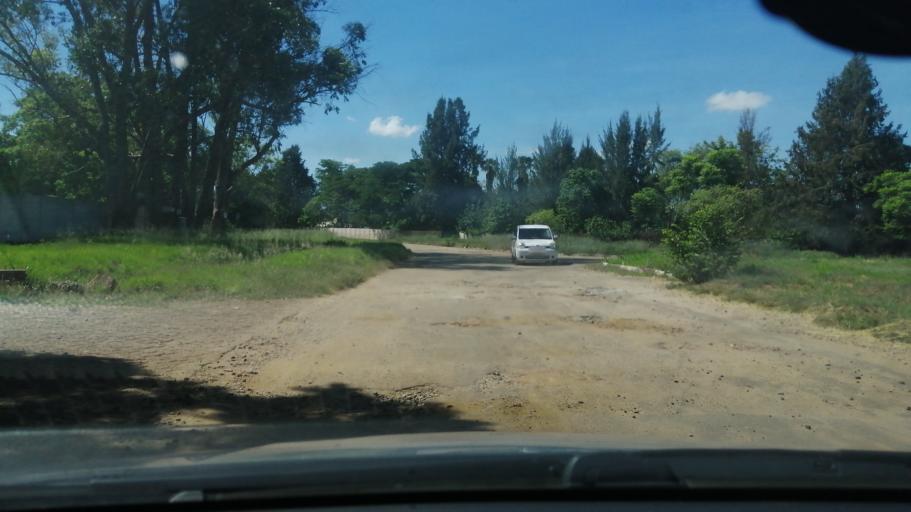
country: ZW
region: Harare
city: Epworth
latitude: -17.8167
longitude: 31.1288
